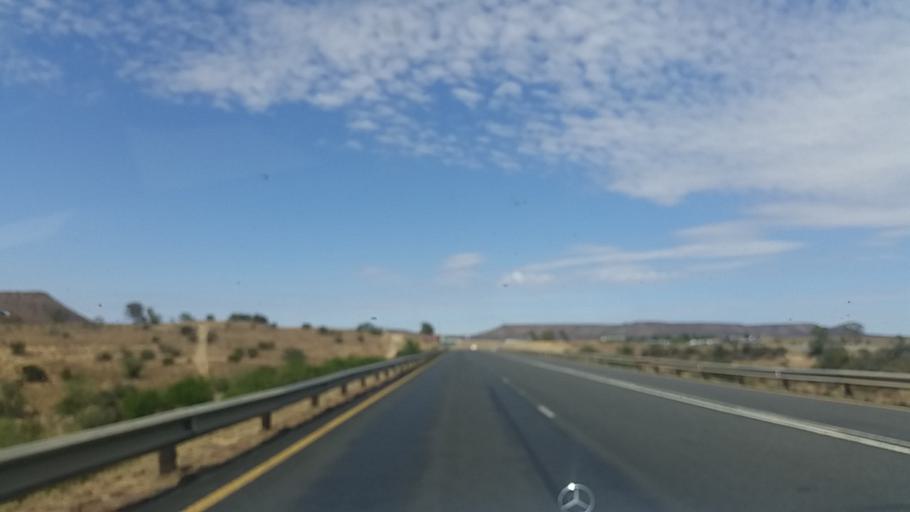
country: ZA
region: Northern Cape
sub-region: Pixley ka Seme District Municipality
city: Colesberg
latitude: -30.7202
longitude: 25.0921
